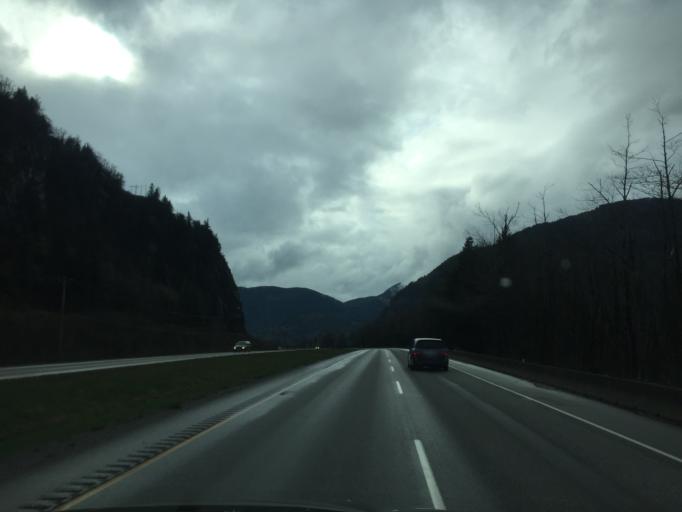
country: CA
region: British Columbia
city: Hope
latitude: 49.3630
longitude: -121.5576
